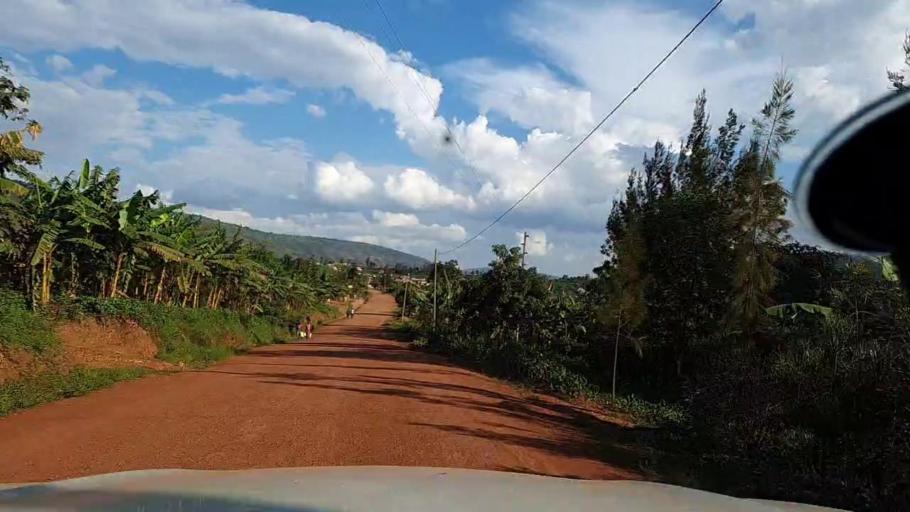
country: RW
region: Kigali
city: Kigali
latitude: -1.8919
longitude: 29.9582
